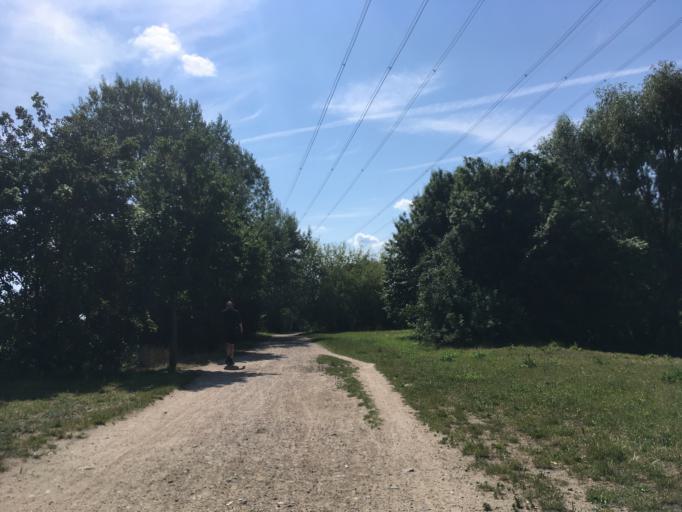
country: DE
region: Brandenburg
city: Ahrensfelde
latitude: 52.5610
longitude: 13.5787
